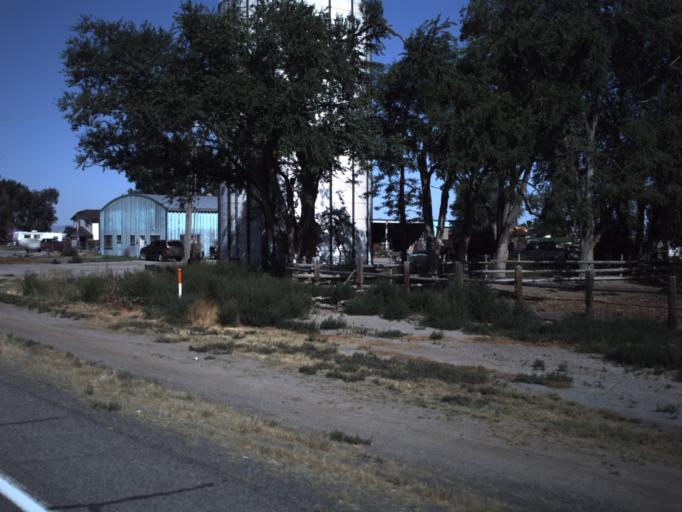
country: US
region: Utah
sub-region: Millard County
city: Delta
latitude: 39.3308
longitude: -112.6589
